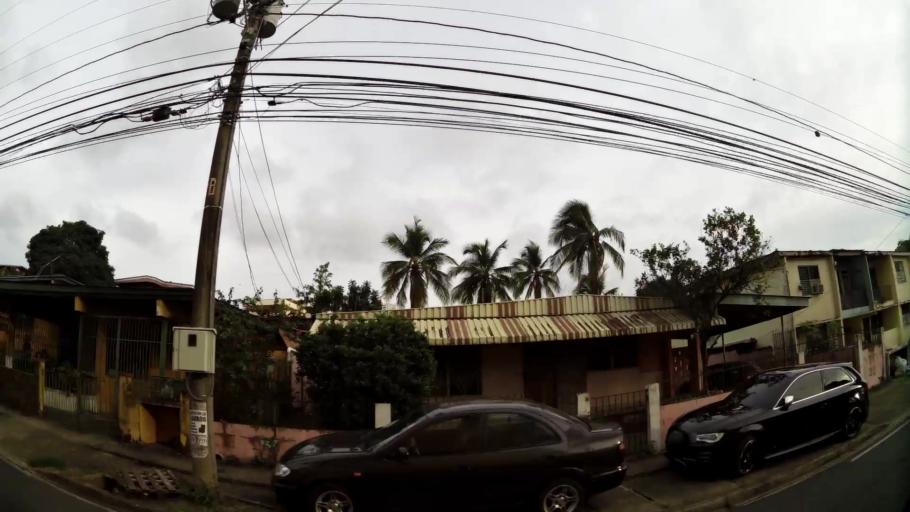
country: PA
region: Panama
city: Panama
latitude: 8.9976
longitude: -79.5170
